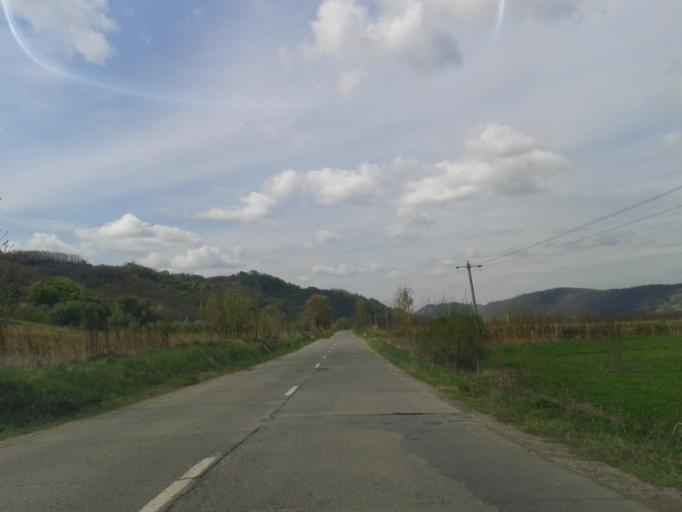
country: RO
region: Sibiu
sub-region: Comuna Axente Sever
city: Axente Sever
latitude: 46.1112
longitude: 24.2039
